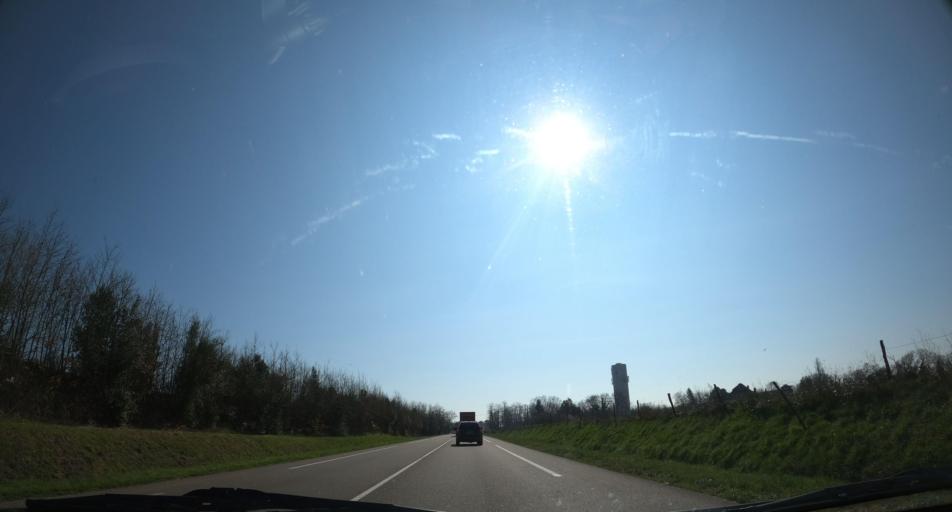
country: FR
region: Aquitaine
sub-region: Departement des Landes
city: Saint-Pierre-du-Mont
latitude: 43.8786
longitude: -0.5240
